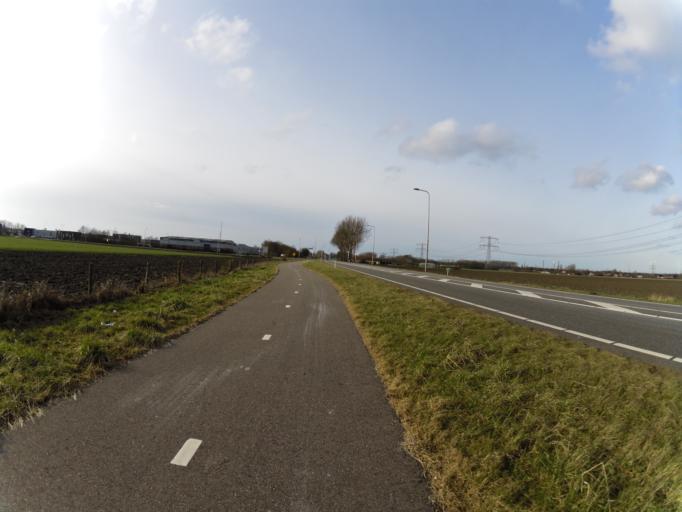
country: NL
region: South Holland
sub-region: Gemeente Brielle
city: Brielle
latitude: 51.9111
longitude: 4.1237
